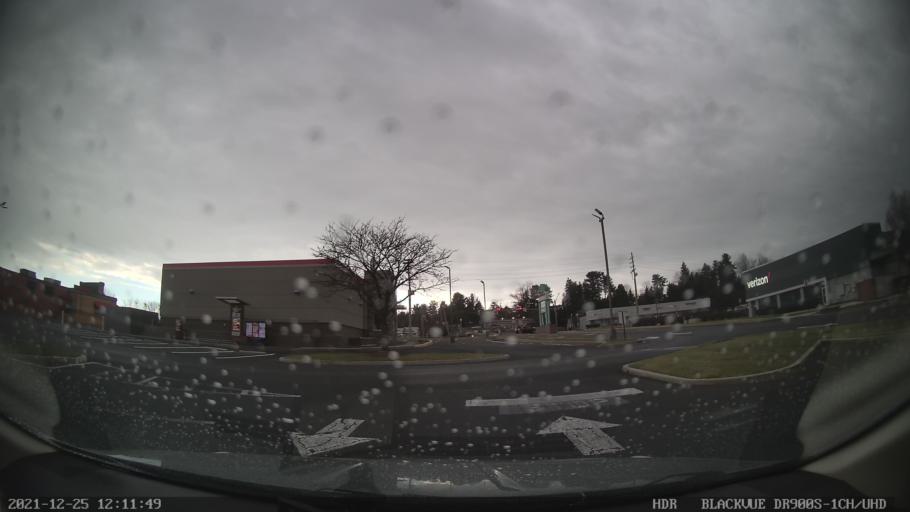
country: US
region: Maryland
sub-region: Frederick County
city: Frederick
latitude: 39.4178
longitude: -77.4412
